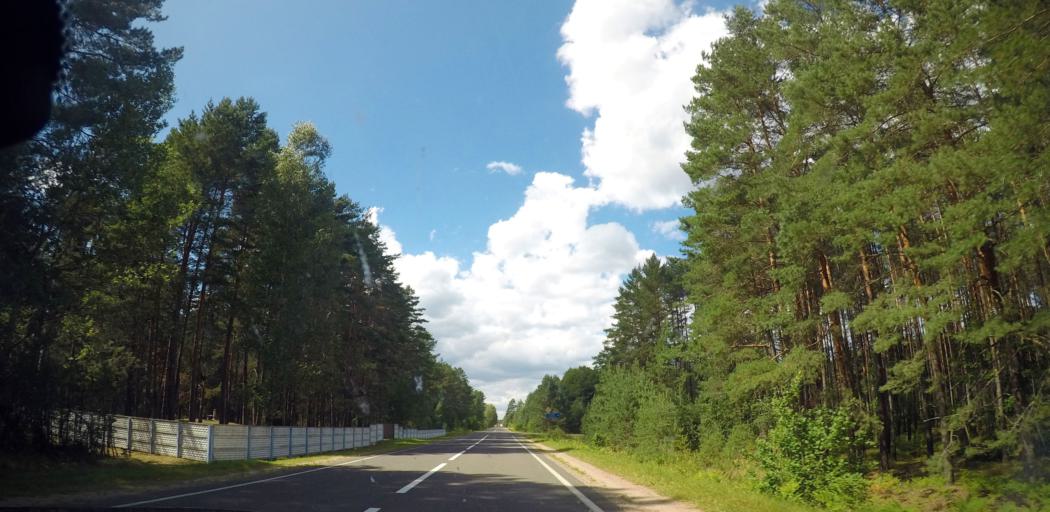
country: LT
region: Alytaus apskritis
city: Druskininkai
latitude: 53.8762
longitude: 24.1487
